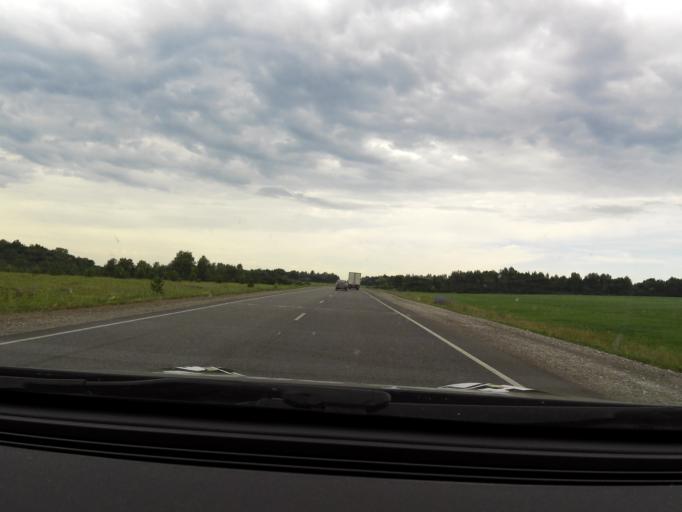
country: RU
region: Bashkortostan
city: Kudeyevskiy
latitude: 54.8161
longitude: 56.7015
